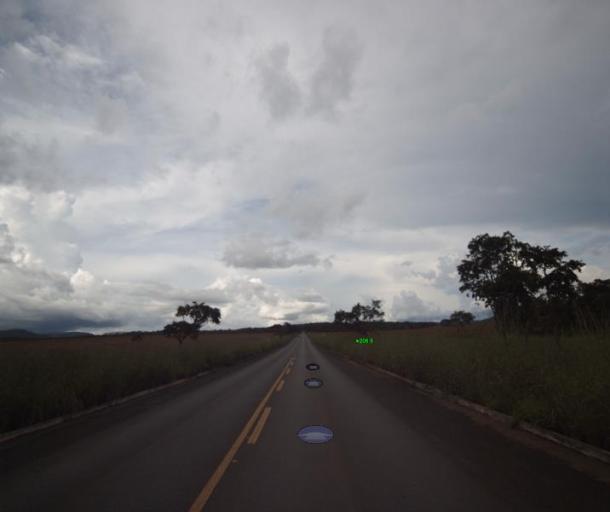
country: BR
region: Goias
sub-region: Niquelandia
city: Niquelandia
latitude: -14.5018
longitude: -48.5140
